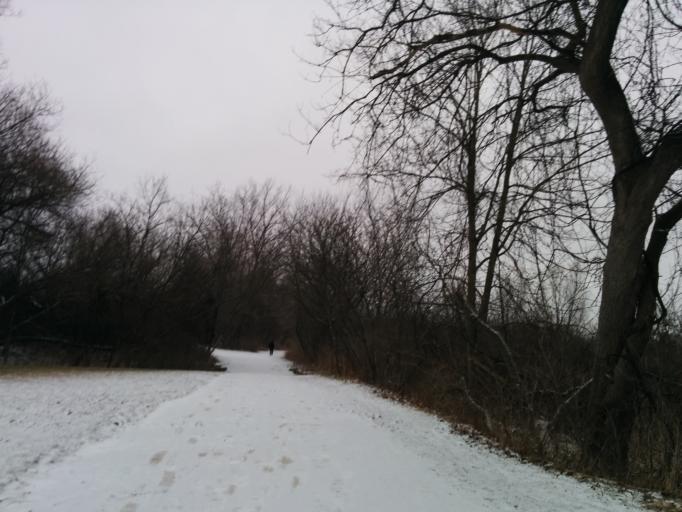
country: CA
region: Ontario
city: Mississauga
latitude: 43.5509
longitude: -79.6566
